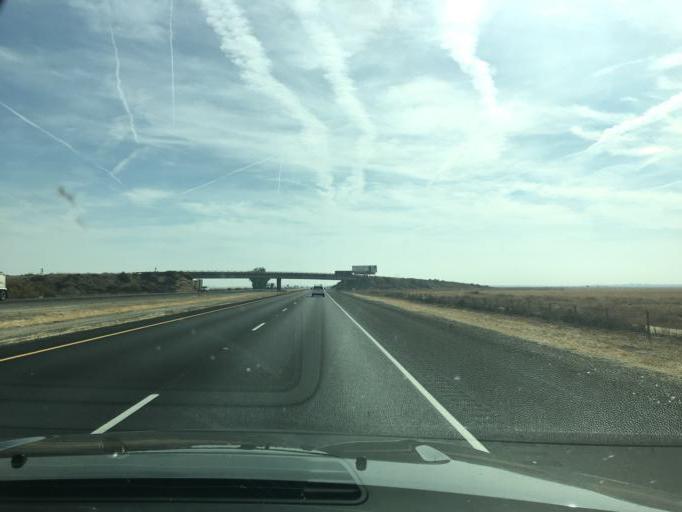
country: US
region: California
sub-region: Kern County
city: Lost Hills
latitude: 35.6685
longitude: -119.6923
